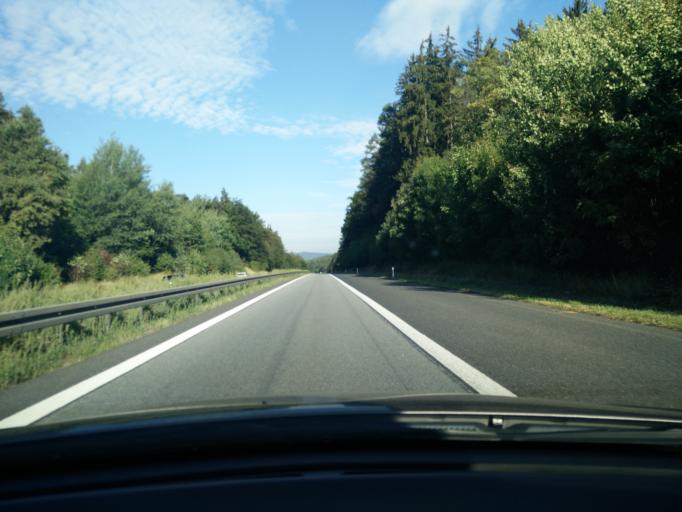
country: DE
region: Bavaria
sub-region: Upper Bavaria
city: Denkendorf
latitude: 48.9700
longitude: 11.4115
